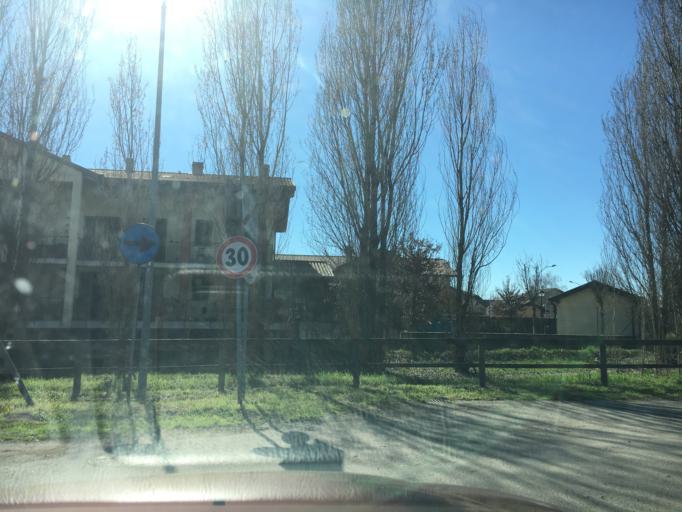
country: IT
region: Lombardy
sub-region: Citta metropolitana di Milano
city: Cusago
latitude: 45.4582
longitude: 9.0473
